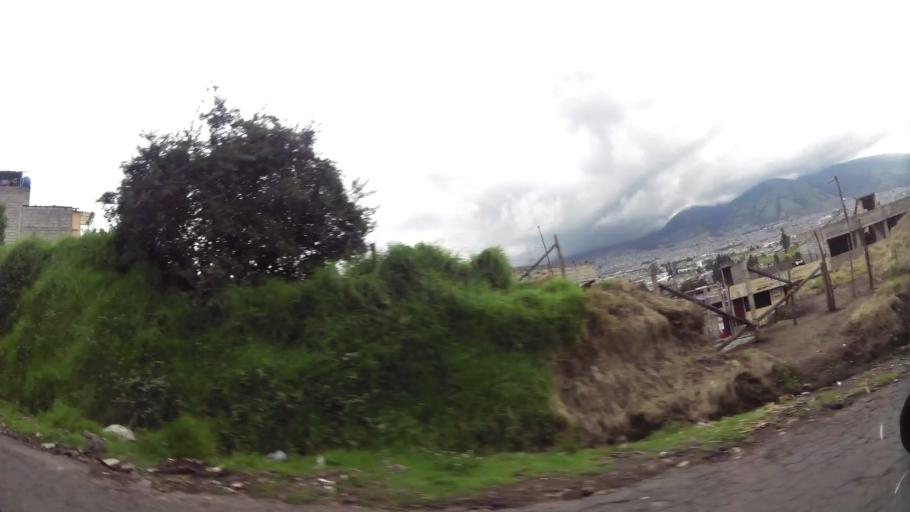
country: EC
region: Pichincha
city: Sangolqui
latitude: -0.3169
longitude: -78.5334
